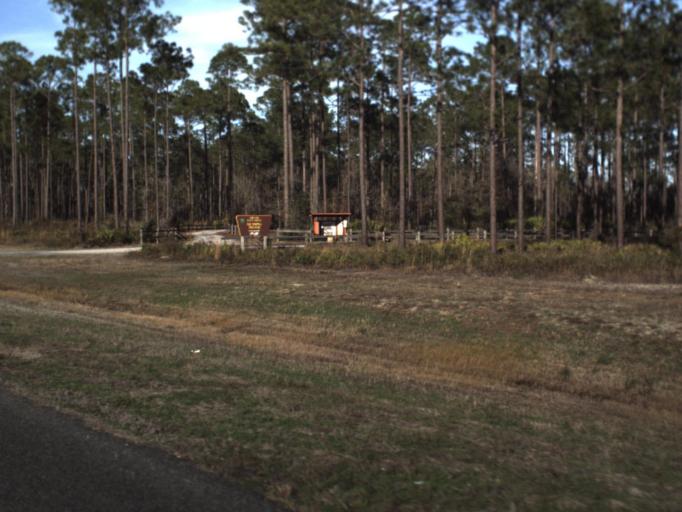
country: US
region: Florida
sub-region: Bay County
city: Laguna Beach
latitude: 30.3976
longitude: -85.8718
